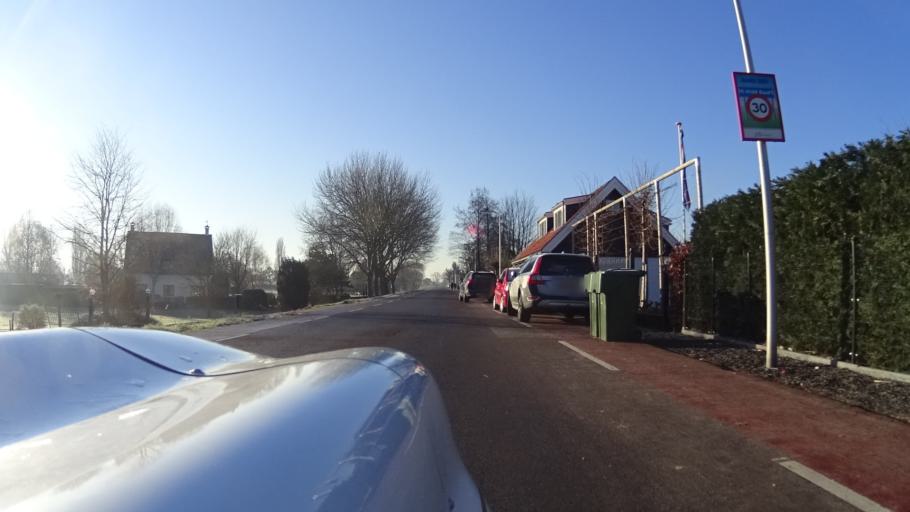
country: NL
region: South Holland
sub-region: Gemeente Oud-Beijerland
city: Oud-Beijerland
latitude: 51.8147
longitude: 4.4374
